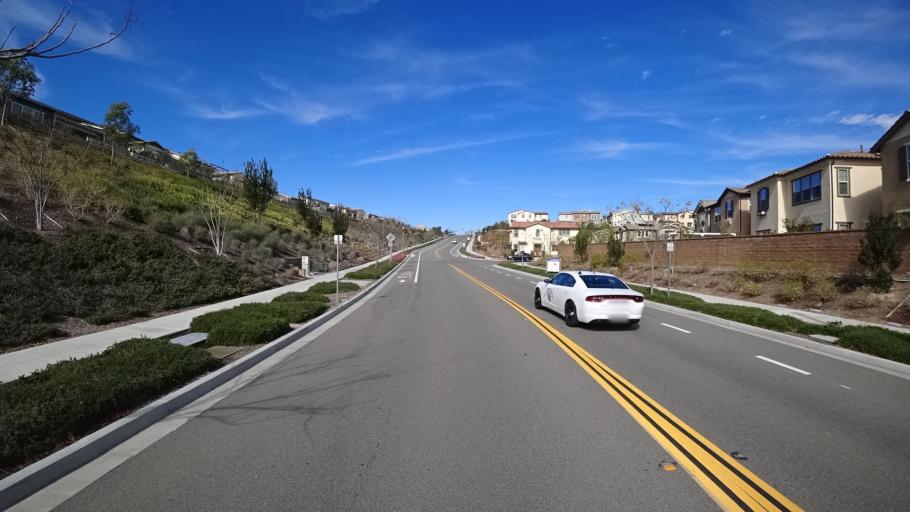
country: US
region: California
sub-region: Orange County
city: Ladera Ranch
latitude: 33.5432
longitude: -117.5958
